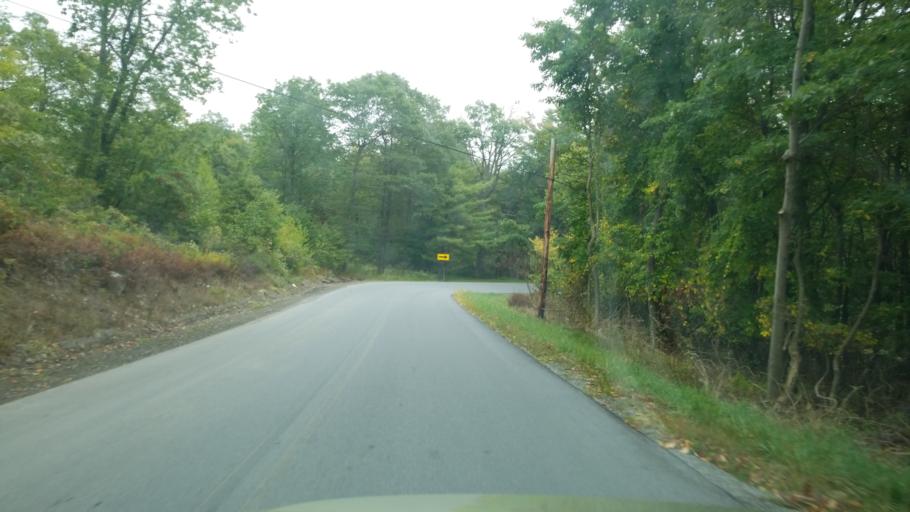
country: US
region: Pennsylvania
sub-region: Clearfield County
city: Curwensville
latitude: 41.0281
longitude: -78.5564
